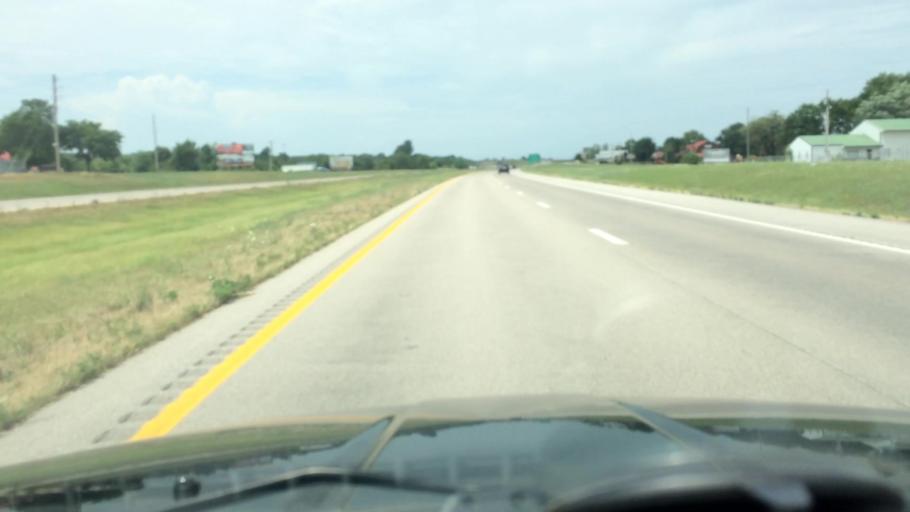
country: US
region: Missouri
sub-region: Polk County
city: Bolivar
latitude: 37.5635
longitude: -93.3930
